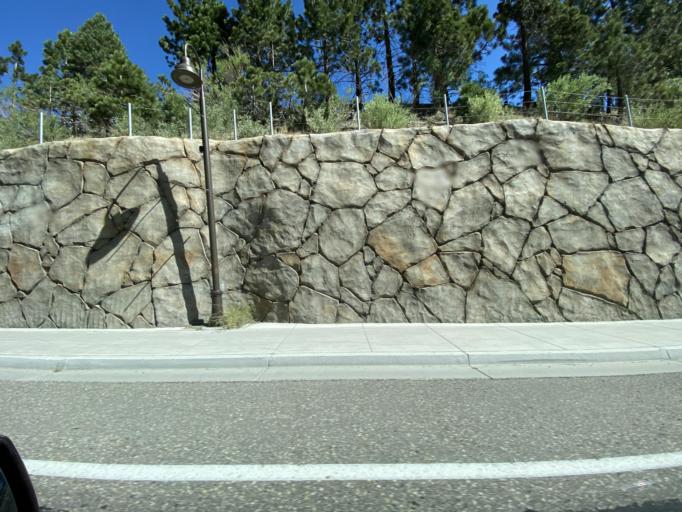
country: US
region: California
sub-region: Mono County
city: Mammoth Lakes
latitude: 37.6488
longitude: -118.9787
